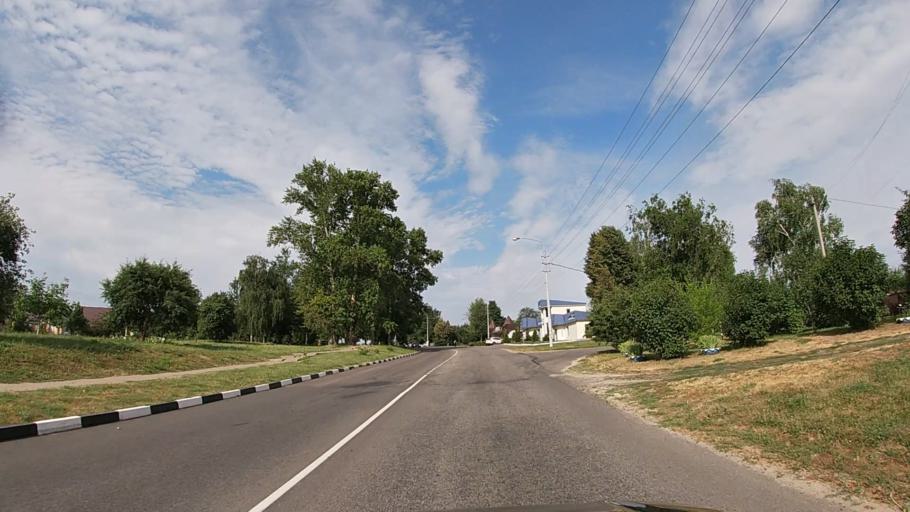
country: RU
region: Belgorod
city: Krasnaya Yaruga
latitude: 50.8010
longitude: 35.6673
